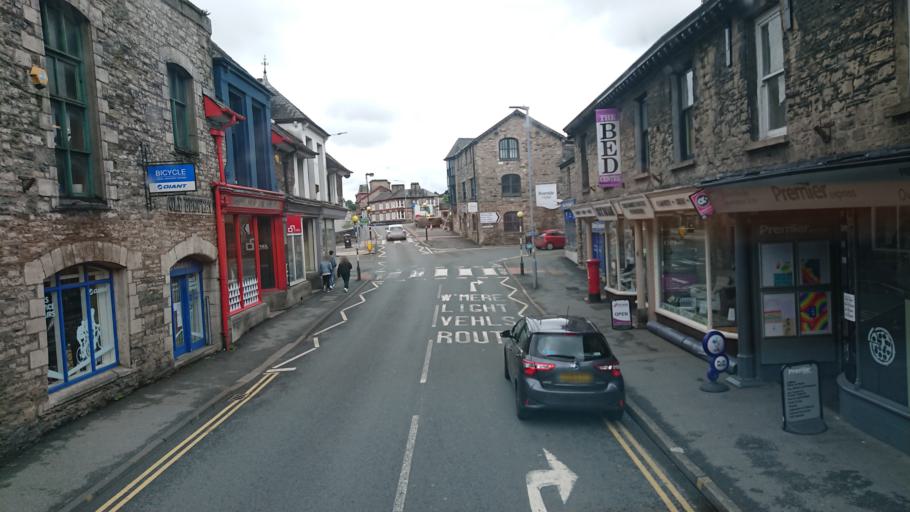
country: GB
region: England
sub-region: Cumbria
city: Kendal
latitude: 54.3307
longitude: -2.7409
